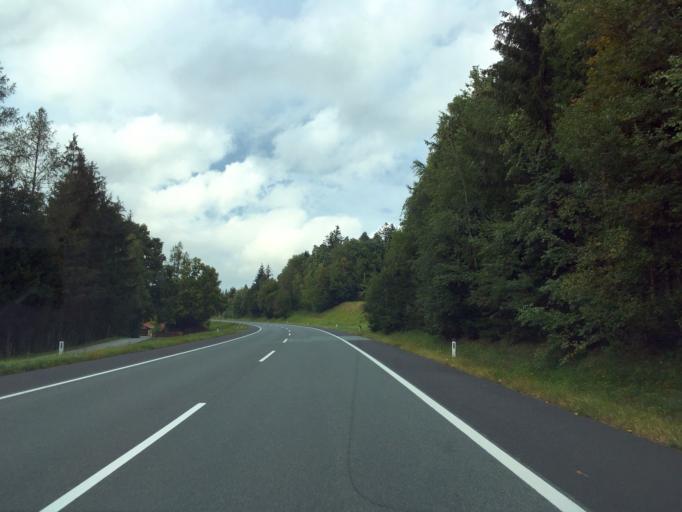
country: AT
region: Styria
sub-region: Politischer Bezirk Hartberg-Fuerstenfeld
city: Pinggau
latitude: 47.4520
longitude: 16.0730
